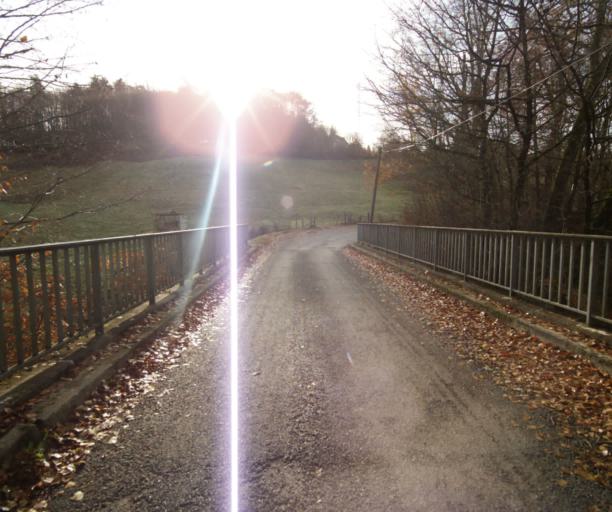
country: FR
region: Limousin
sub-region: Departement de la Correze
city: Chameyrat
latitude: 45.2262
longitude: 1.7254
